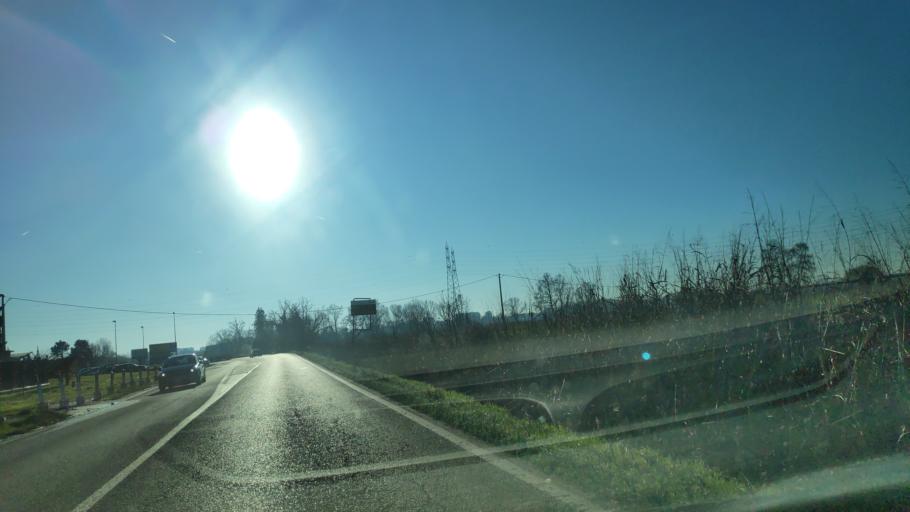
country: IT
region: Lombardy
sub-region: Citta metropolitana di Milano
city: Colturano
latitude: 45.3748
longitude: 9.3366
